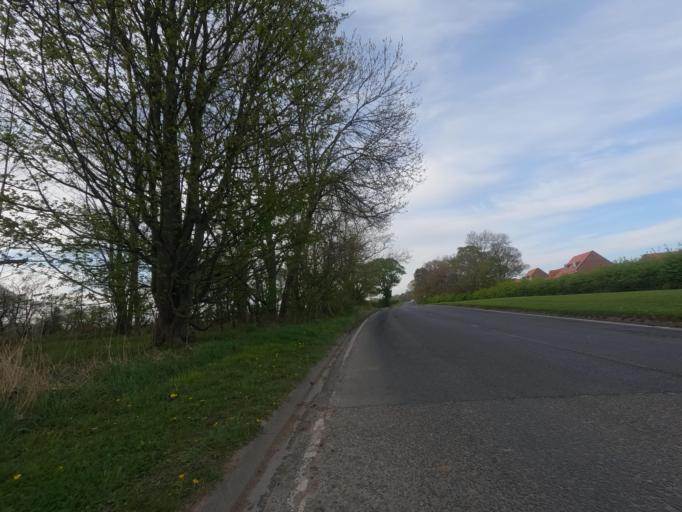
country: GB
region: England
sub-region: Newcastle upon Tyne
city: Dinnington
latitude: 55.0320
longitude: -1.6657
